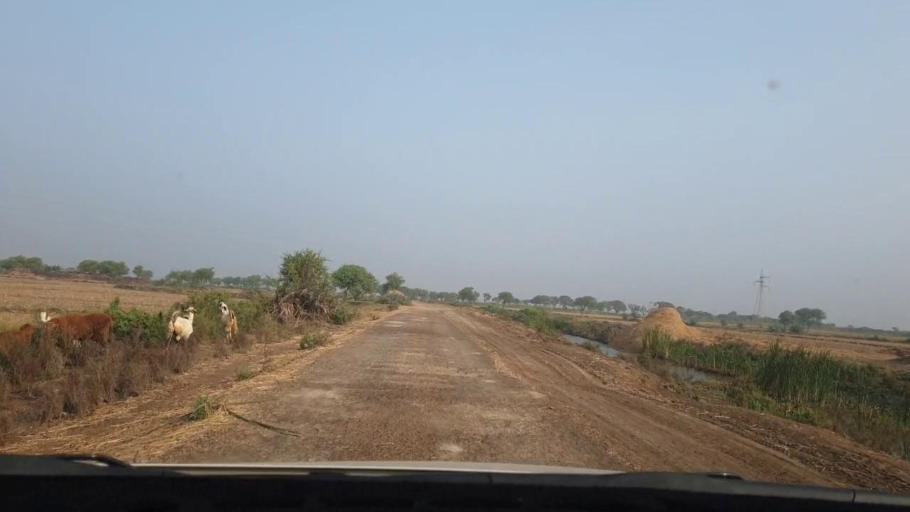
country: PK
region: Sindh
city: Tando Muhammad Khan
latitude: 25.0825
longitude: 68.4861
